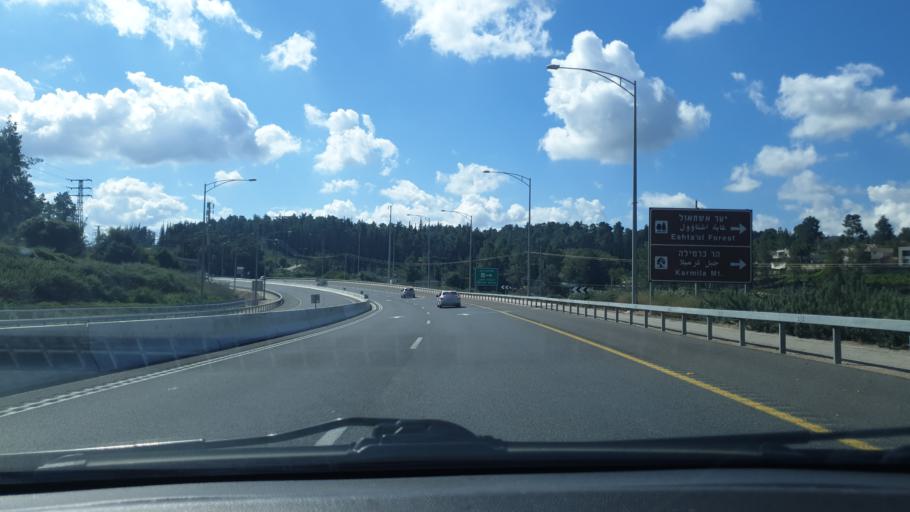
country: IL
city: Mevo horon
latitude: 31.8018
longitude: 35.0150
